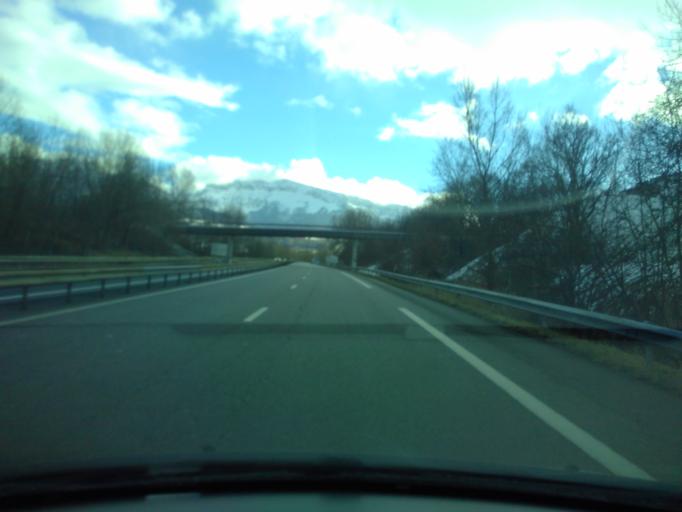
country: FR
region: Rhone-Alpes
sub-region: Departement de la Haute-Savoie
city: Etaux
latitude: 46.0657
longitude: 6.2898
